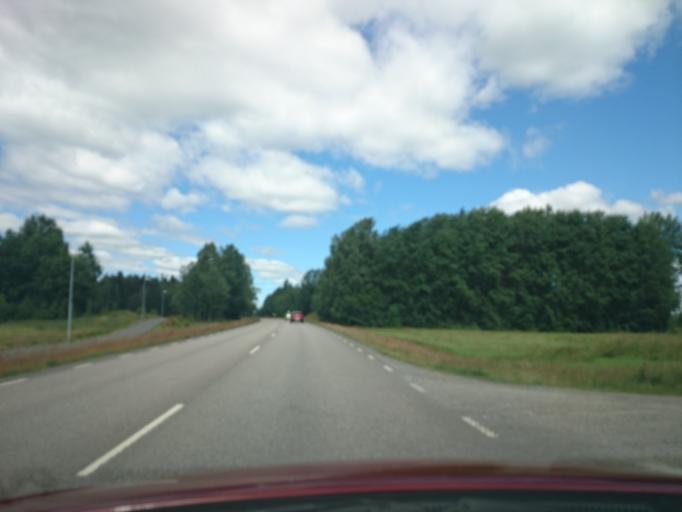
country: SE
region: Vaestra Goetaland
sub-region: Lerums Kommun
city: Grabo
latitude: 57.8197
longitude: 12.2995
